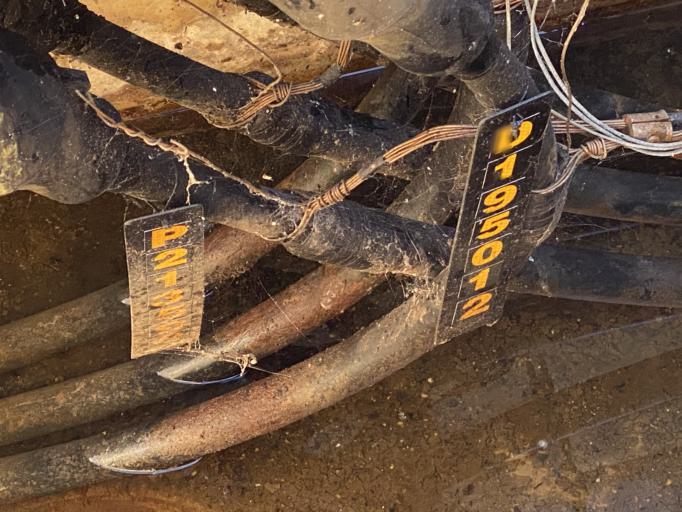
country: US
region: California
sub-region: San Diego County
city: Ramona
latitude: 33.0260
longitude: -116.8708
